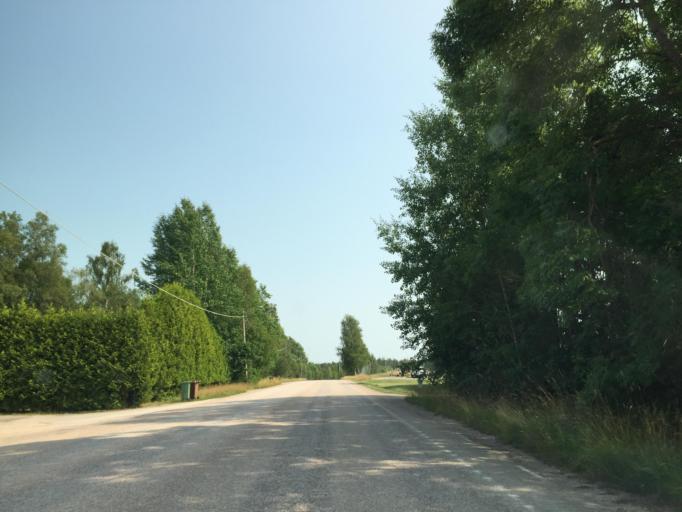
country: SE
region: Vaestra Goetaland
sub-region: Trollhattan
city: Sjuntorp
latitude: 58.3293
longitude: 12.1461
